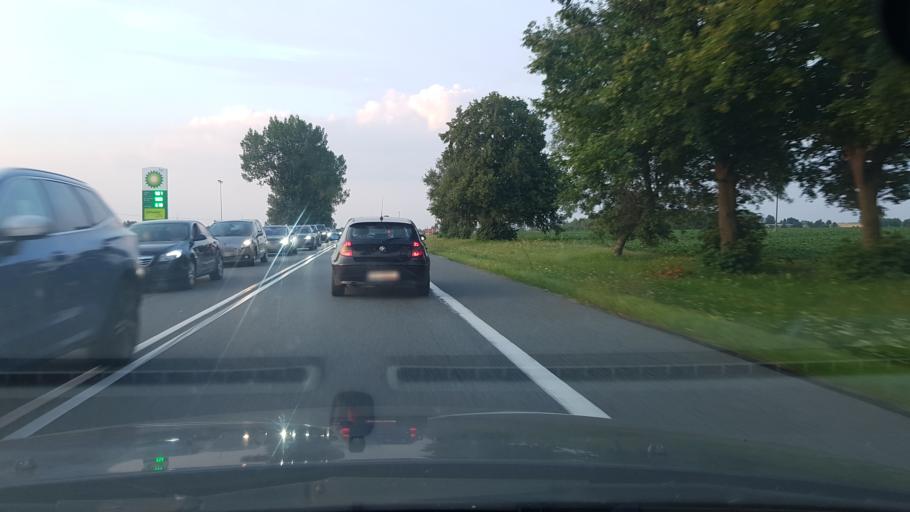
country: PL
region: Masovian Voivodeship
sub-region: Powiat mlawski
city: Wieczfnia Koscielna
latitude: 53.1711
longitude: 20.4209
